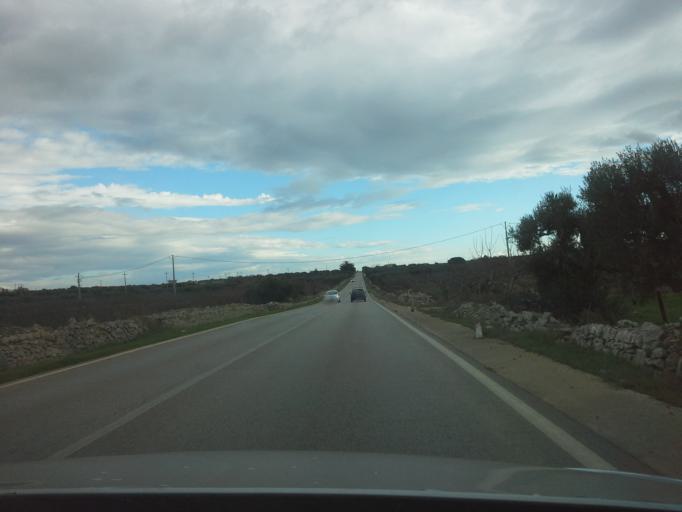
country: IT
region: Apulia
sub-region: Provincia di Bari
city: Turi
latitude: 40.8883
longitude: 17.0464
